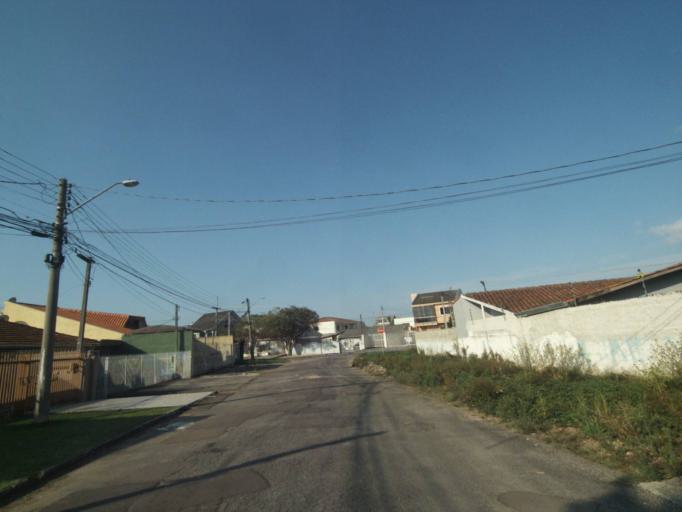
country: BR
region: Parana
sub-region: Curitiba
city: Curitiba
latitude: -25.4846
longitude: -49.3346
